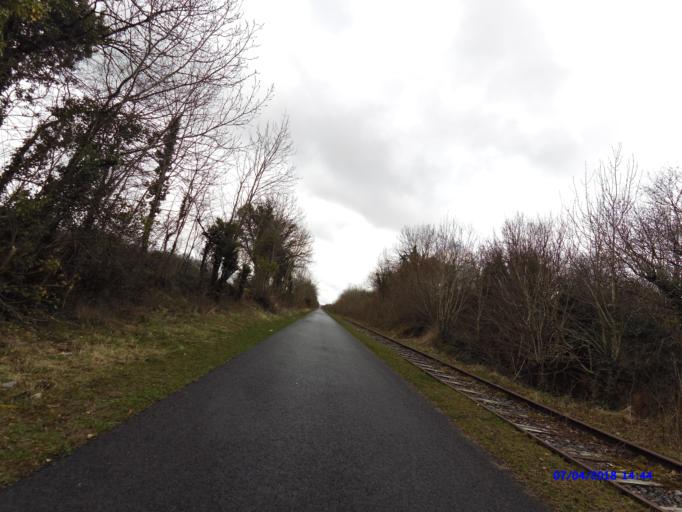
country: IE
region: Leinster
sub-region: An Iarmhi
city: Athlone
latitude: 53.4191
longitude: -7.8811
